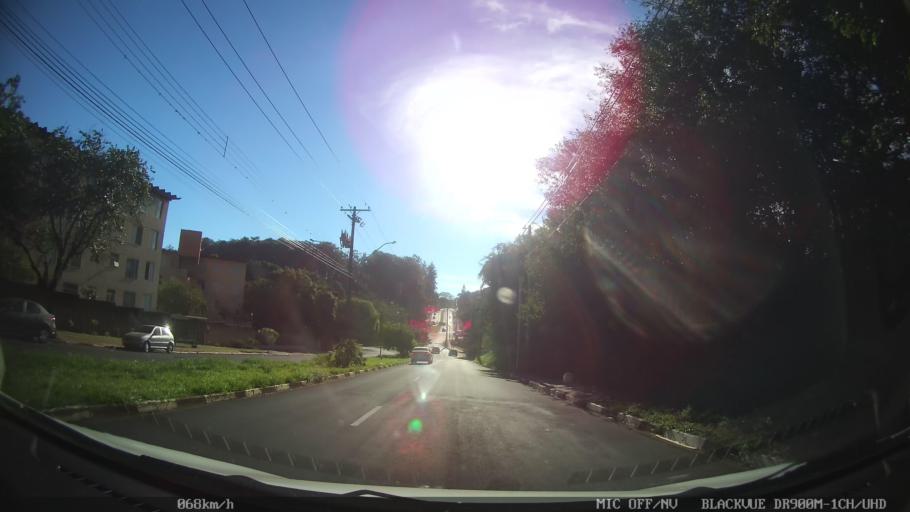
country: BR
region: Sao Paulo
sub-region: Araraquara
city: Araraquara
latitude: -21.7586
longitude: -48.1781
